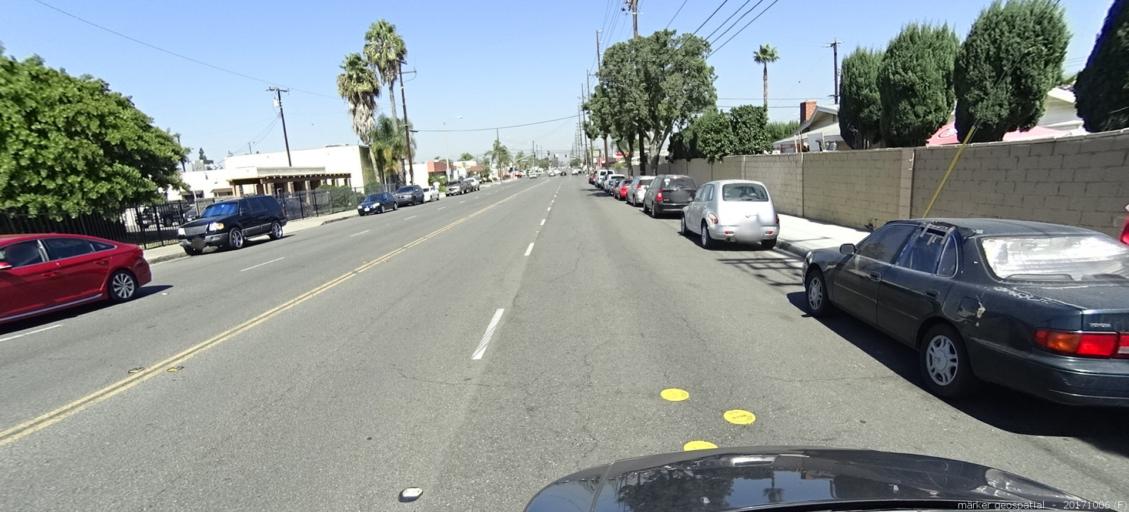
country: US
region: California
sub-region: Orange County
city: Stanton
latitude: 33.8013
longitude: -117.9844
